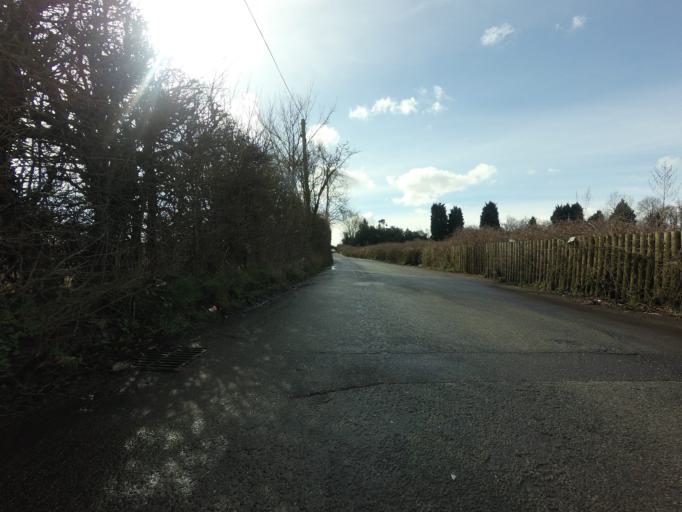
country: GB
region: England
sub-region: Greater London
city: Orpington
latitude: 51.3890
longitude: 0.1341
